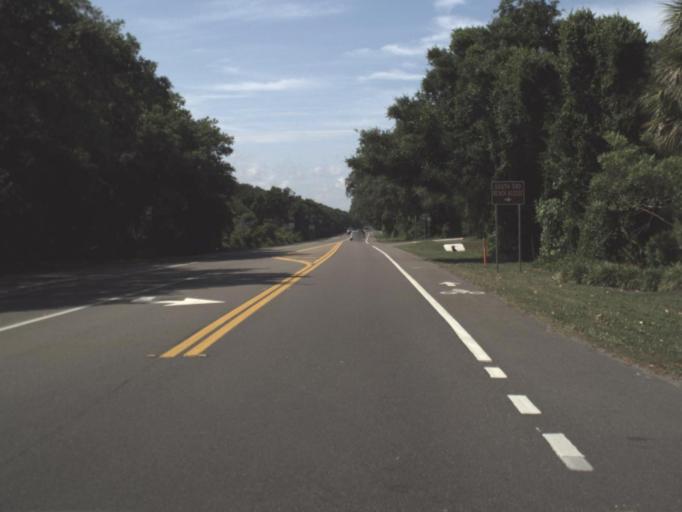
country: US
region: Florida
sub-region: Nassau County
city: Fernandina Beach
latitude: 30.5372
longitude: -81.4417
